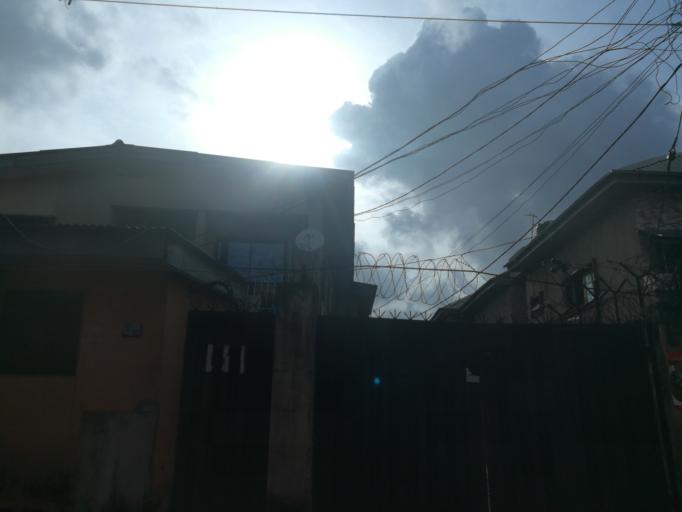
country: NG
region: Lagos
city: Somolu
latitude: 6.5418
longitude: 3.3810
